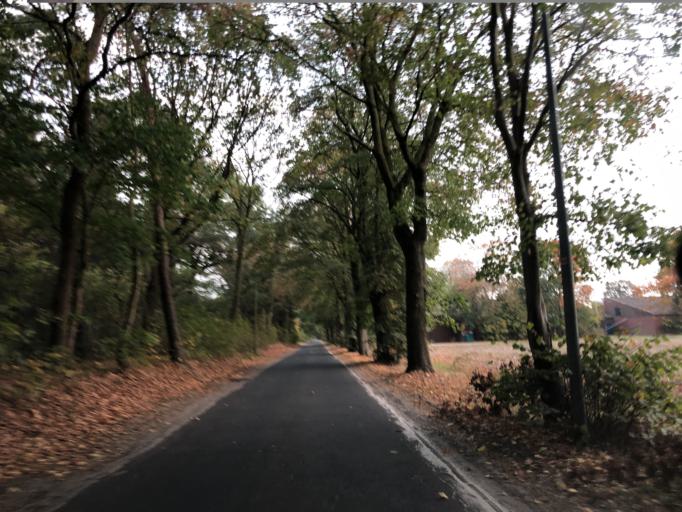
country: DE
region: Lower Saxony
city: Papenburg
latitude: 53.0558
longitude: 7.4105
